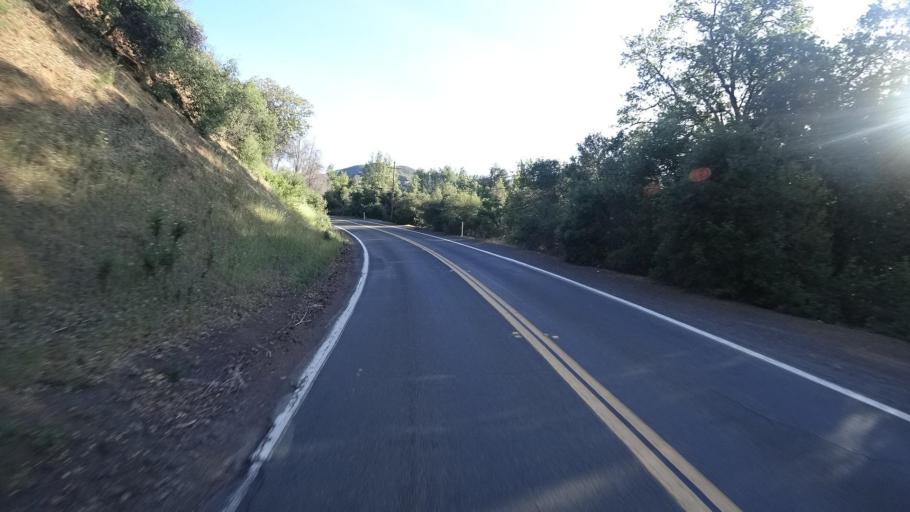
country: US
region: California
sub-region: Lake County
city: North Lakeport
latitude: 39.1202
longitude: -122.9883
